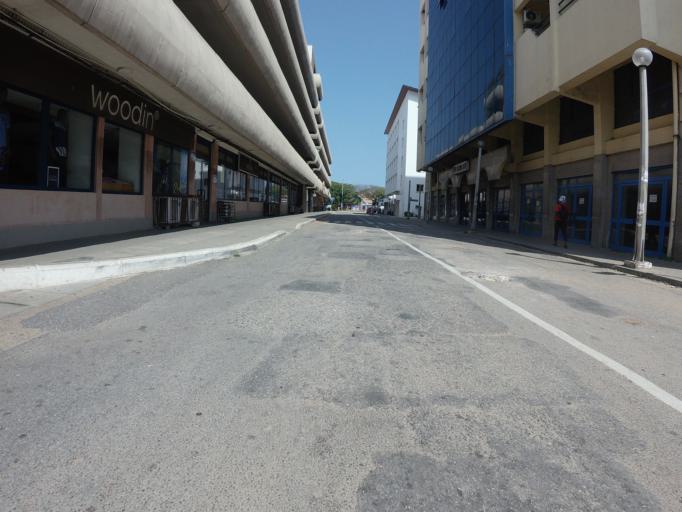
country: GH
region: Greater Accra
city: Accra
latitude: 5.5421
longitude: -0.2073
